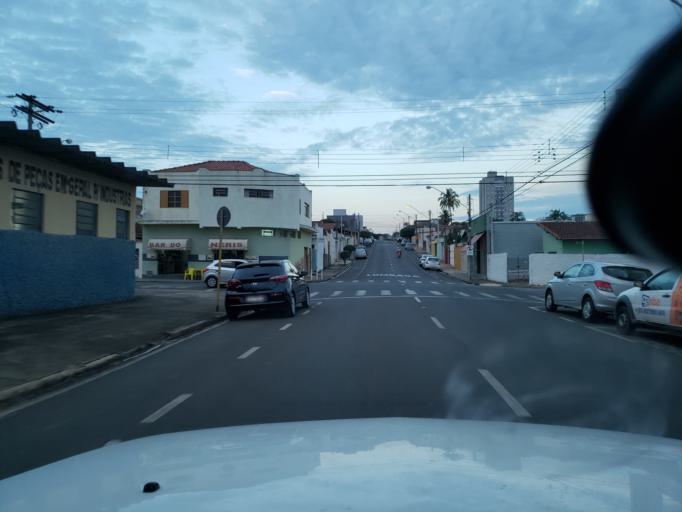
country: BR
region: Sao Paulo
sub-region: Moji-Guacu
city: Mogi-Gaucu
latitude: -22.3642
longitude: -46.9506
